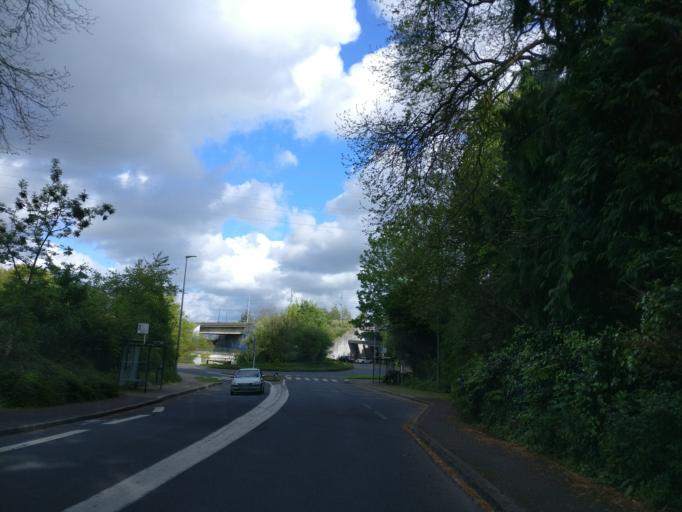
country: FR
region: Brittany
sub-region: Departement du Finistere
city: Le Relecq-Kerhuon
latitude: 48.3974
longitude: -4.4368
